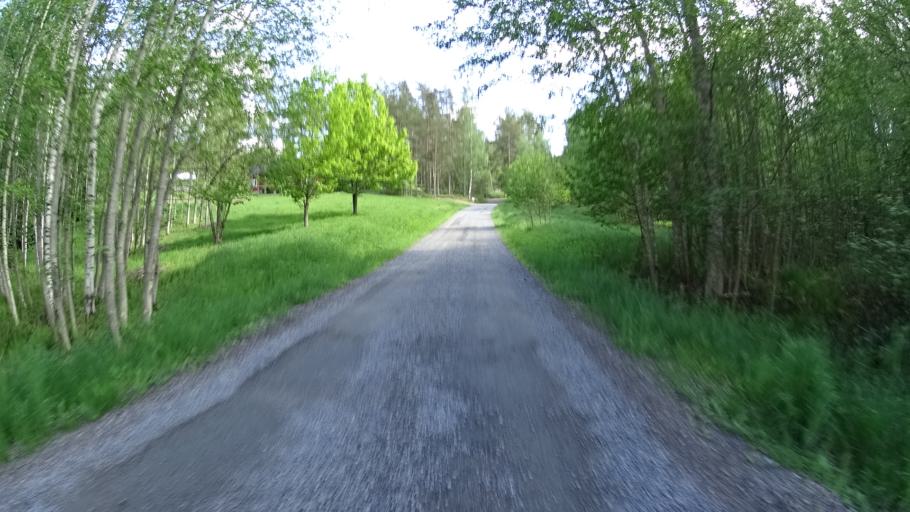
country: FI
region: Varsinais-Suomi
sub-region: Salo
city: Kisko
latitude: 60.1944
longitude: 23.5517
